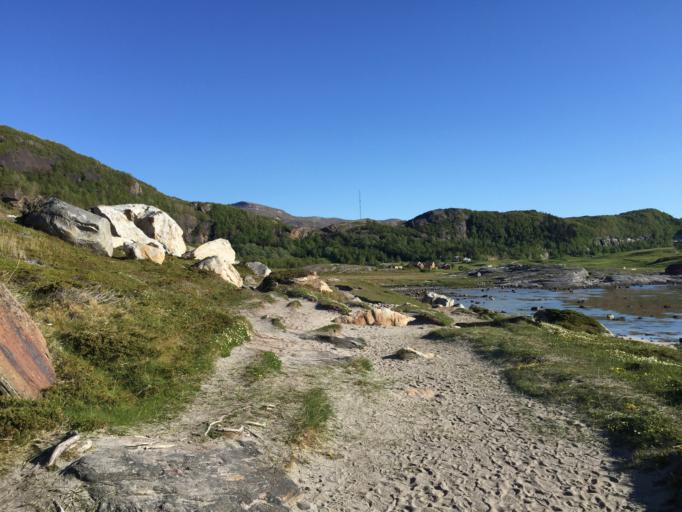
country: NO
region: Nordland
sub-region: Bodo
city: Loding
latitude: 67.4151
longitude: 14.6328
